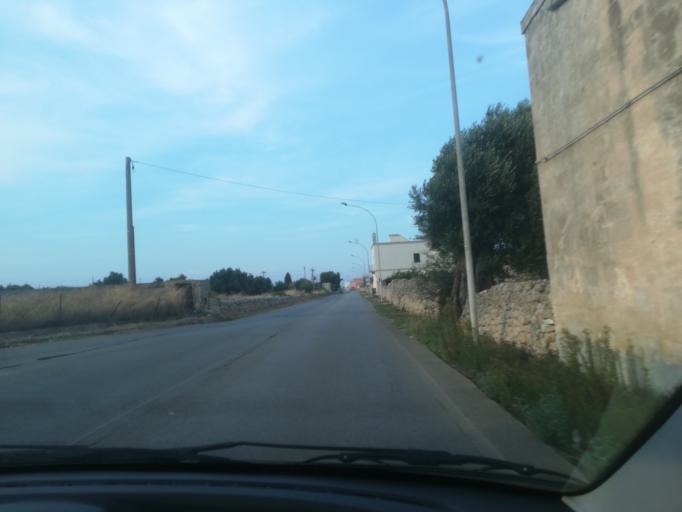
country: IT
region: Apulia
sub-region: Provincia di Bari
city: Monopoli
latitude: 40.9377
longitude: 17.2937
